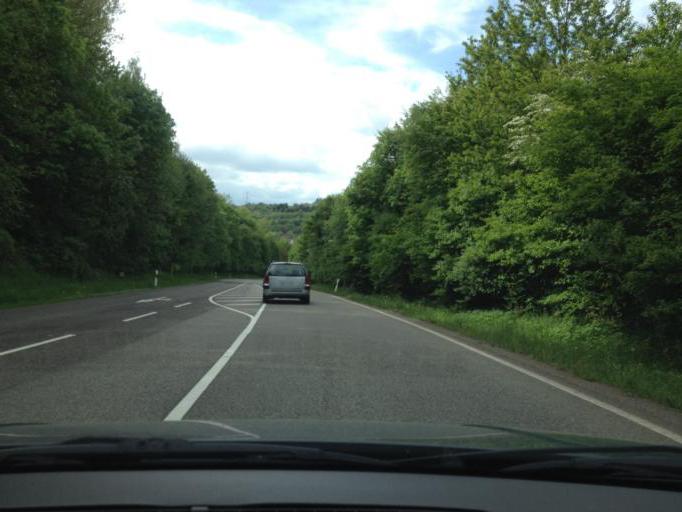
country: DE
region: Saarland
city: Hangard
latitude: 49.3712
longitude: 7.2036
